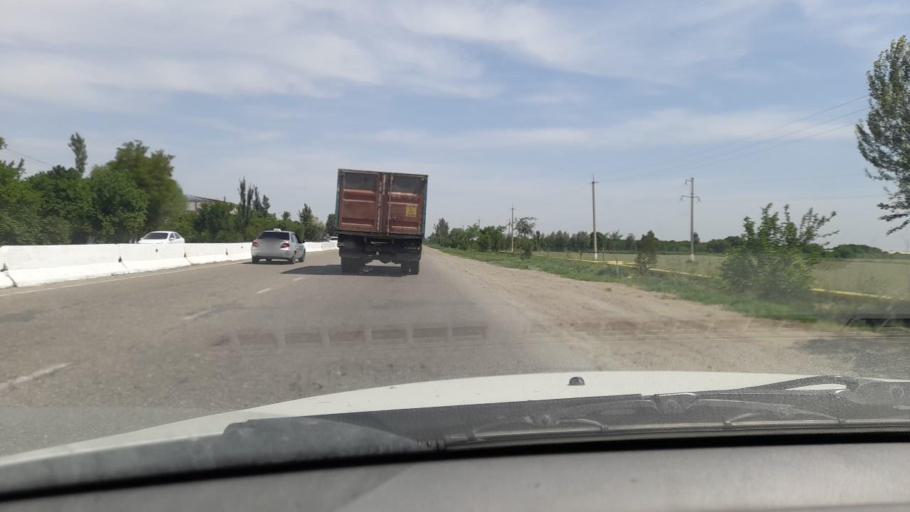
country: UZ
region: Bukhara
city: Wobkent
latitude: 40.0007
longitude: 64.5163
